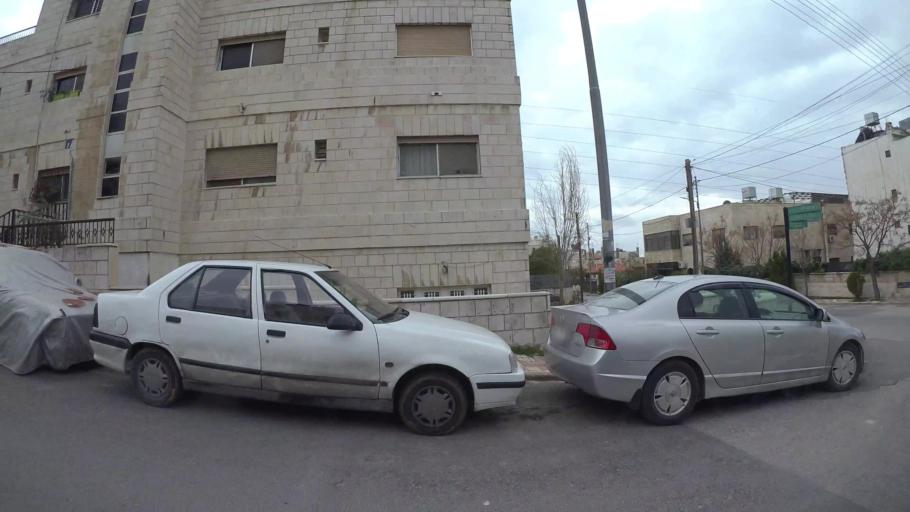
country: JO
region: Amman
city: Wadi as Sir
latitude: 31.9640
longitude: 35.8335
